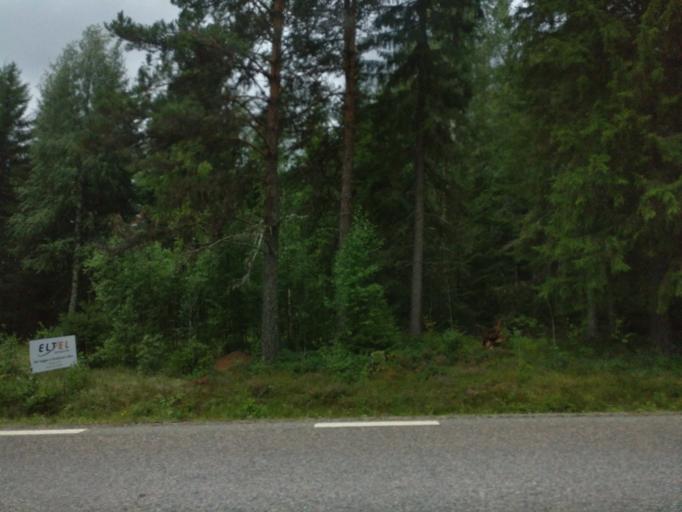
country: SE
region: Vaermland
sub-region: Torsby Kommun
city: Torsby
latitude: 60.7620
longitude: 12.7630
